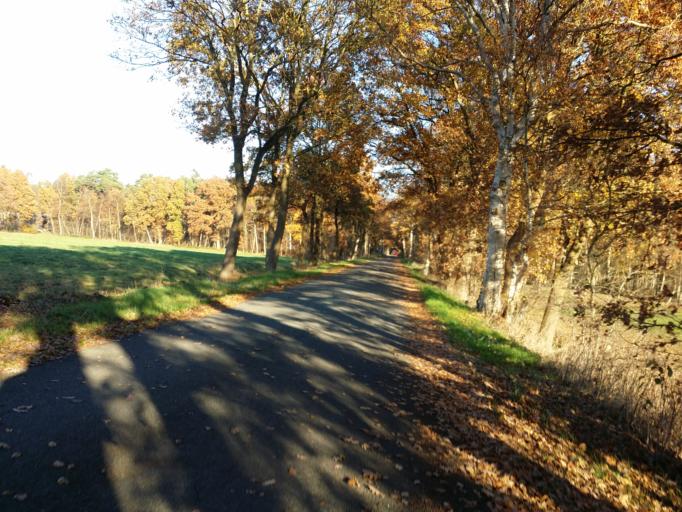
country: DE
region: Lower Saxony
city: Langwedel
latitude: 53.0282
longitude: 9.1837
